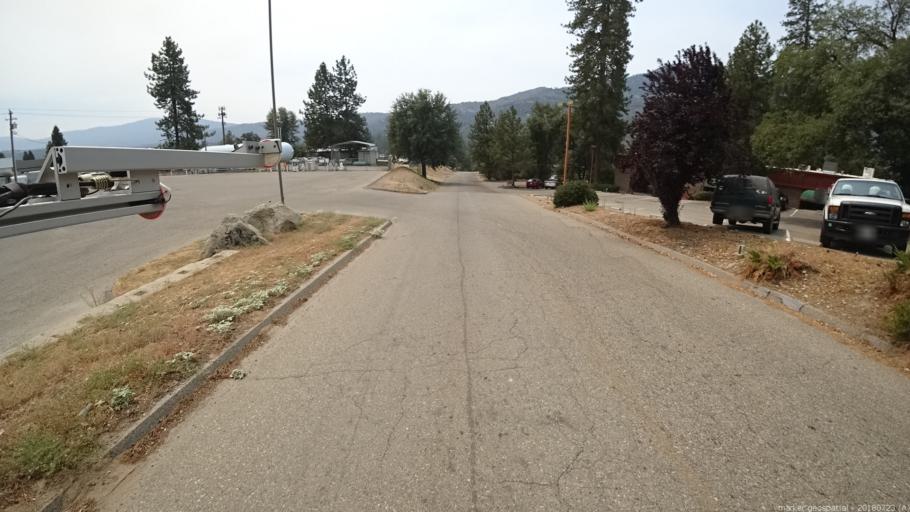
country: US
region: California
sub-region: Madera County
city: Oakhurst
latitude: 37.3355
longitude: -119.6637
